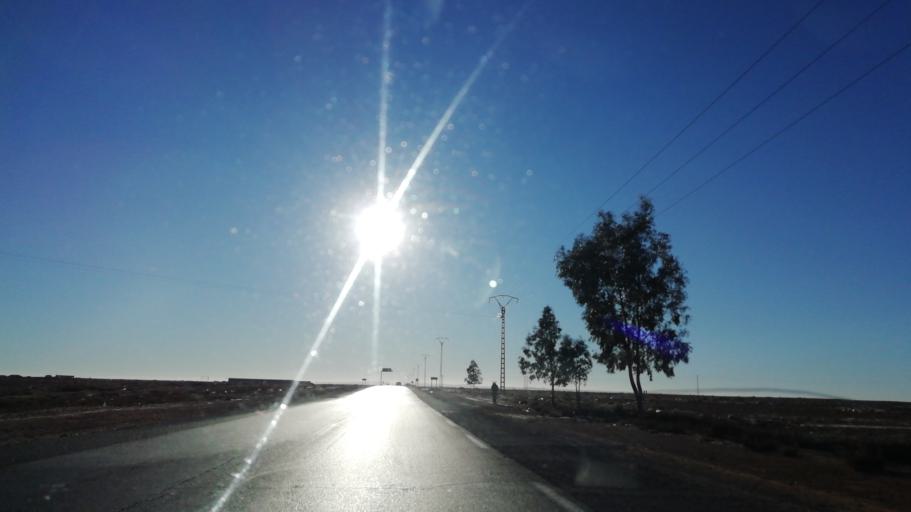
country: DZ
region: Saida
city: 'Ain el Hadjar
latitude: 34.0224
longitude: 0.1018
